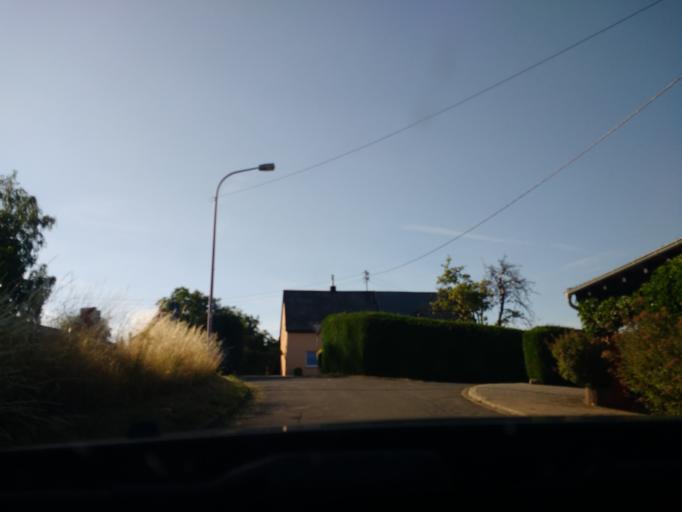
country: DE
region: Rheinland-Pfalz
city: Bleckhausen
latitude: 50.1231
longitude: 6.7790
